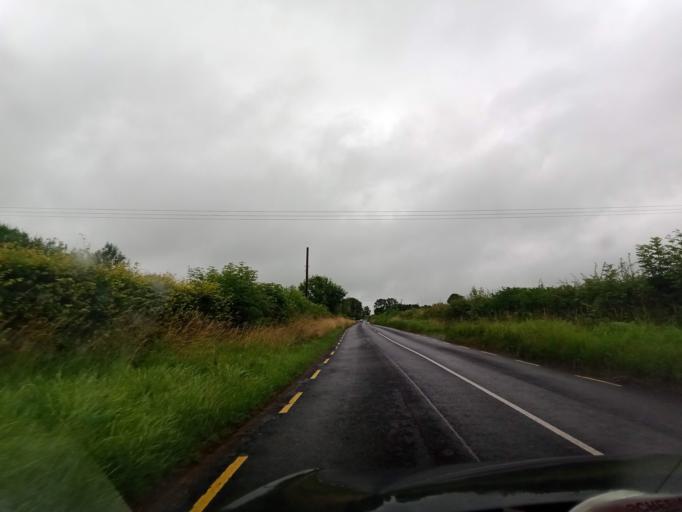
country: IE
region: Leinster
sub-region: Laois
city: Abbeyleix
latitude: 52.9100
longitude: -7.3108
